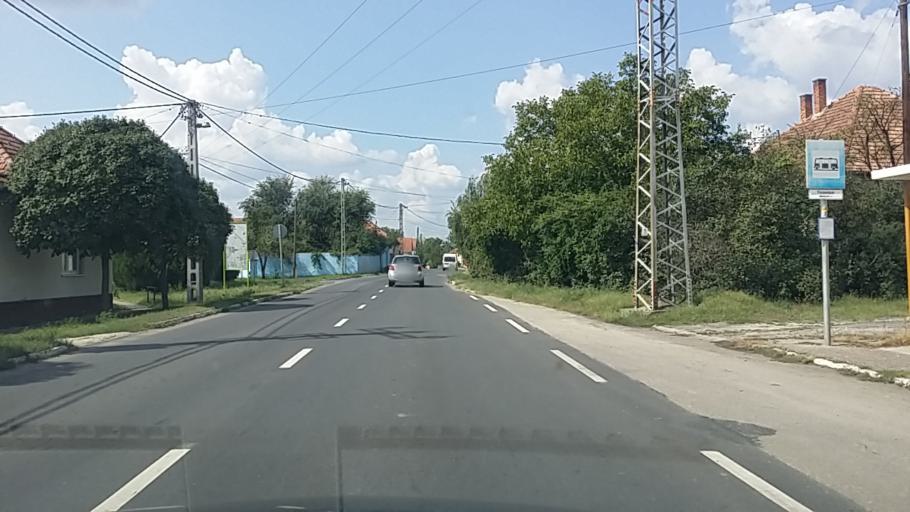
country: HU
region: Bacs-Kiskun
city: Tiszaalpar
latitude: 46.8246
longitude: 19.9835
